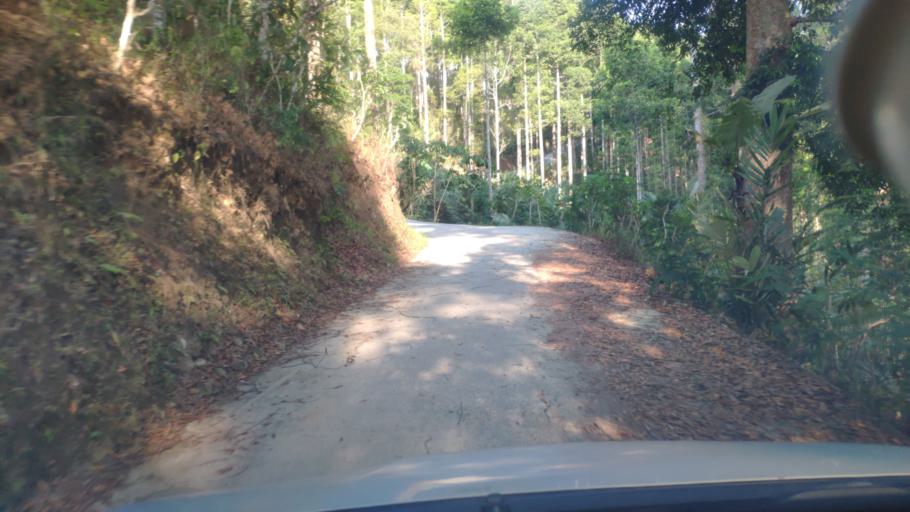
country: ID
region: Central Java
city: Wonosobo
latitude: -7.4184
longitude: 109.7483
